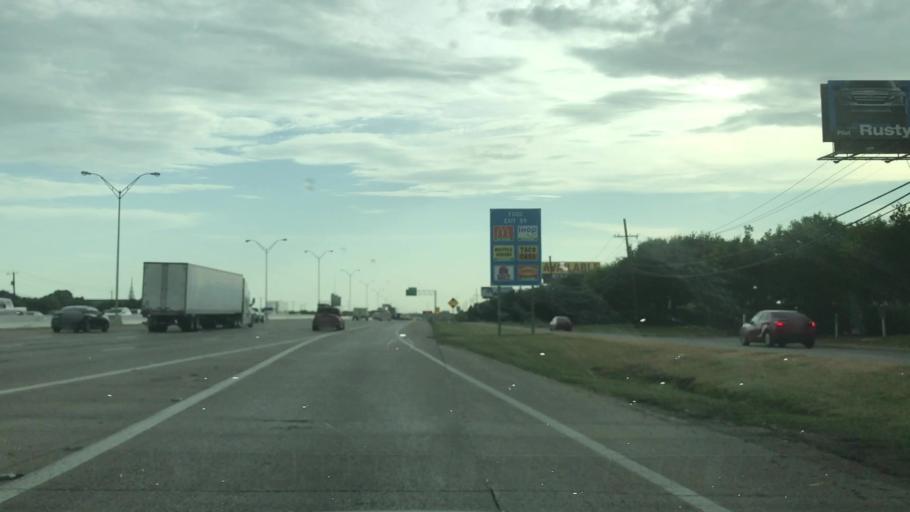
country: US
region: Texas
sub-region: Dallas County
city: Sunnyvale
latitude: 32.8491
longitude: -96.5737
